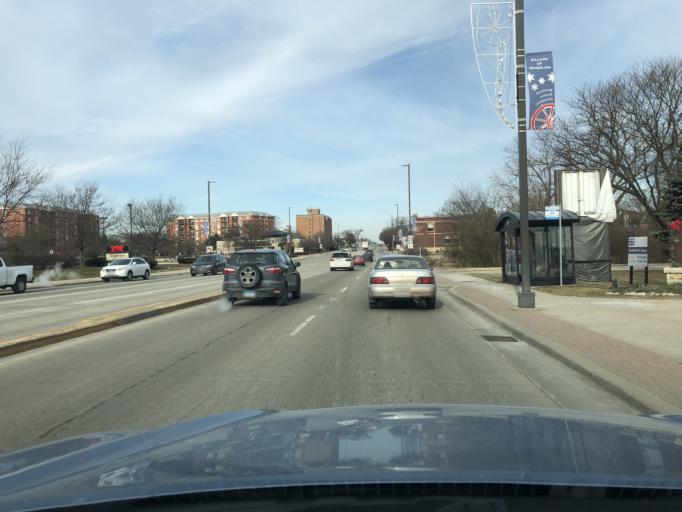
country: US
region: Illinois
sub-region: Cook County
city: Wheeling
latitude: 42.1406
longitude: -87.9080
